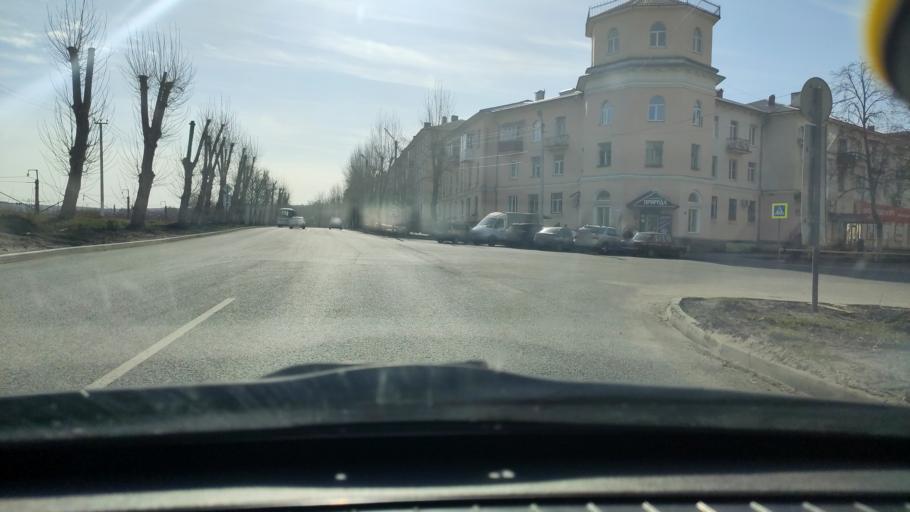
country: RU
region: Samara
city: Zhigulevsk
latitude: 53.4050
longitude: 49.4940
